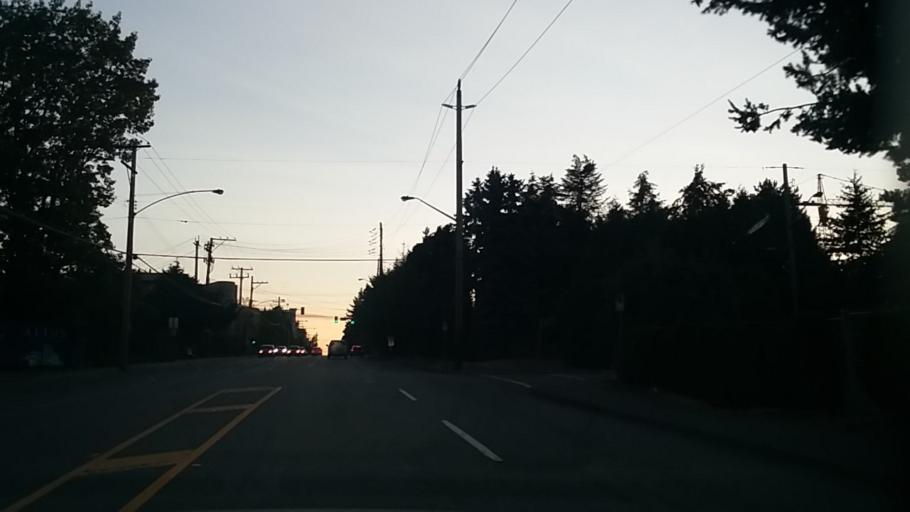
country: CA
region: British Columbia
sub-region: Greater Vancouver Regional District
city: White Rock
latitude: 49.0311
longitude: -122.7882
